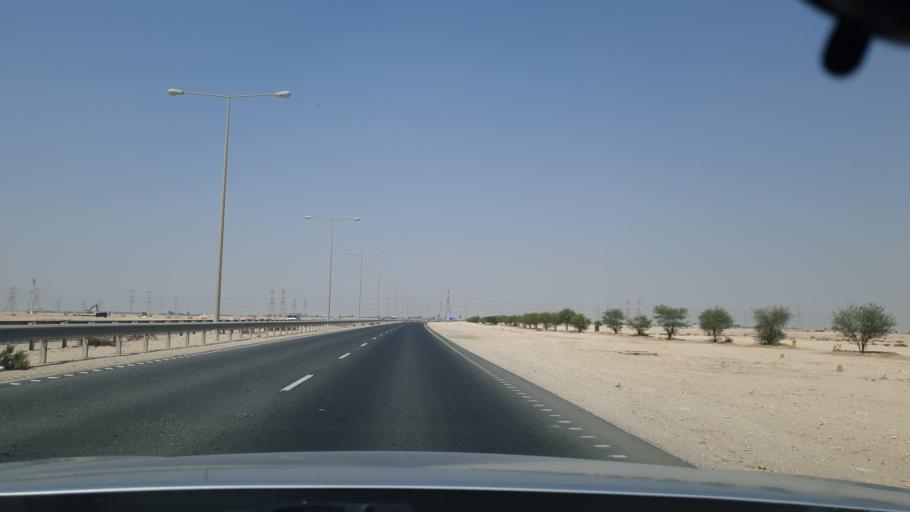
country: QA
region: Al Khawr
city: Al Khawr
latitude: 25.7456
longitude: 51.4820
